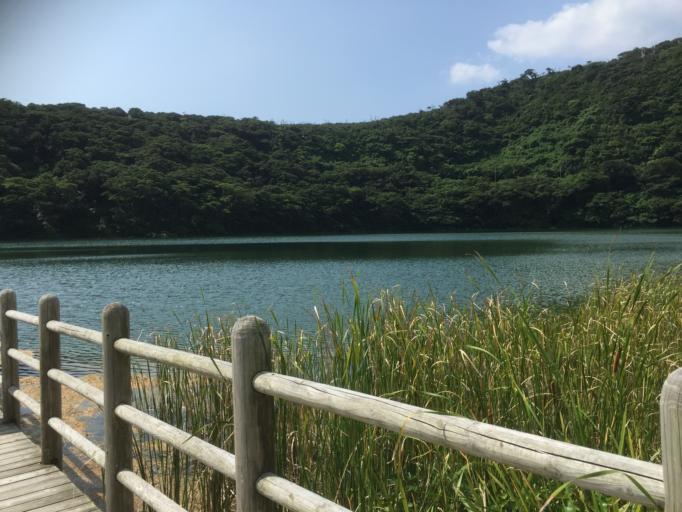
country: JP
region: Shizuoka
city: Shimoda
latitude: 34.0558
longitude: 139.5260
